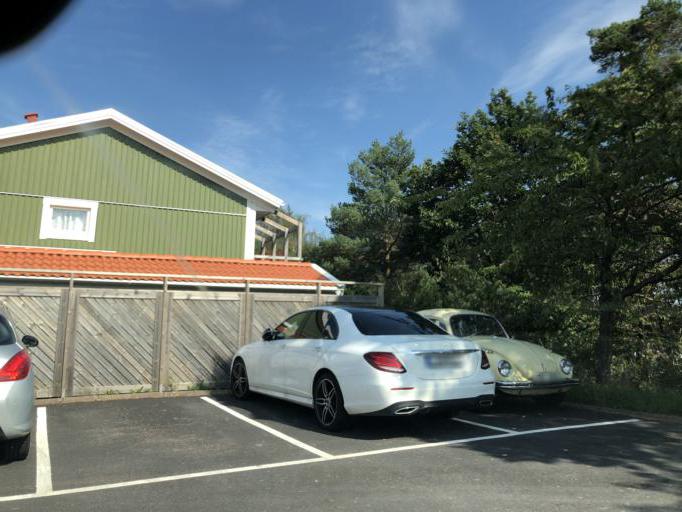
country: SE
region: Vaestra Goetaland
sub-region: Goteborg
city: Goeteborg
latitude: 57.7608
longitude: 11.9630
